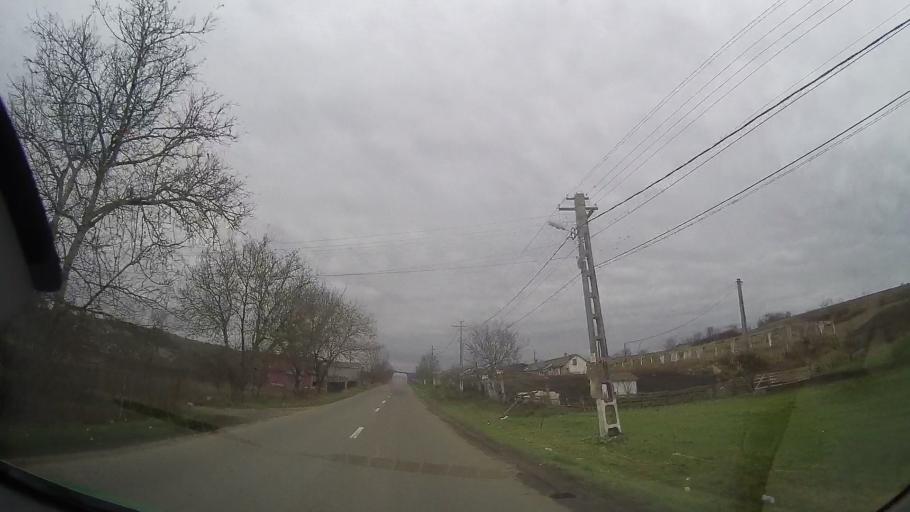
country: RO
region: Mures
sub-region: Comuna Sarmasu
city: Sarmasu
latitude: 46.7888
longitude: 24.2065
